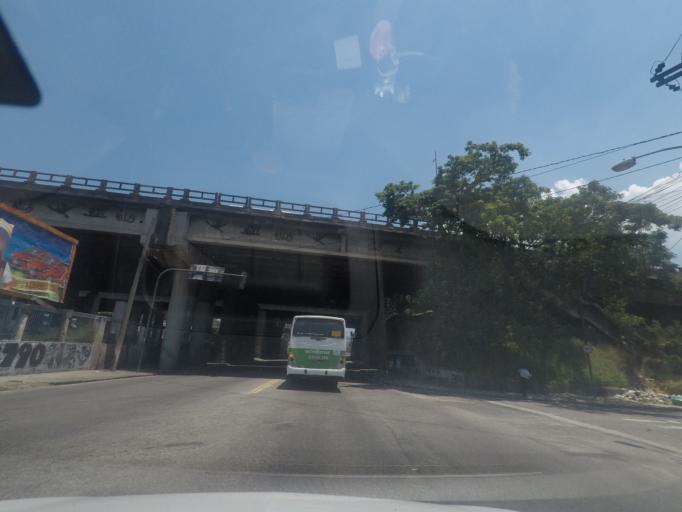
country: BR
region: Rio de Janeiro
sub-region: Duque De Caxias
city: Duque de Caxias
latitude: -22.8150
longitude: -43.3012
